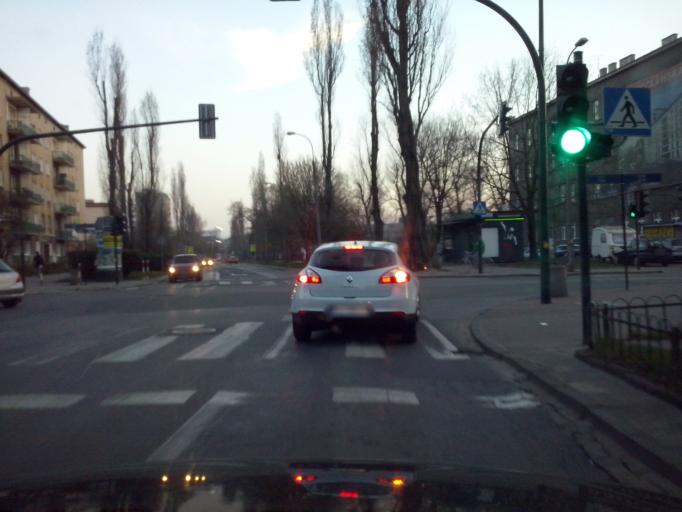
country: PL
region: Lesser Poland Voivodeship
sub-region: Krakow
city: Krakow
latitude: 50.0716
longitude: 19.9145
